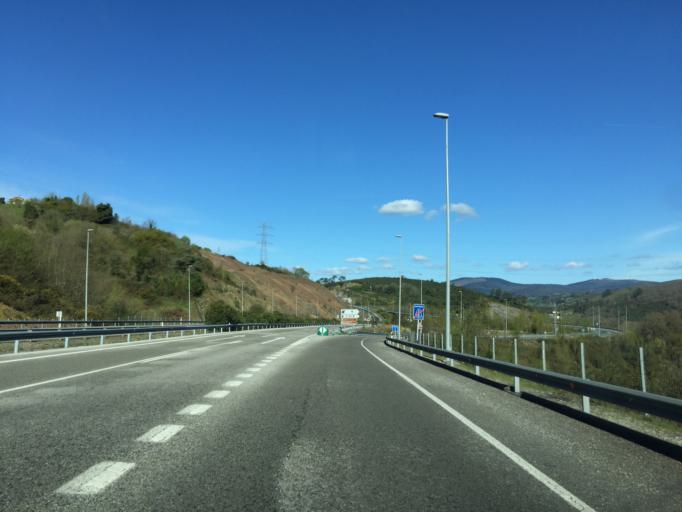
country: ES
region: Asturias
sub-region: Province of Asturias
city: Llanera
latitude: 43.3606
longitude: -5.9466
